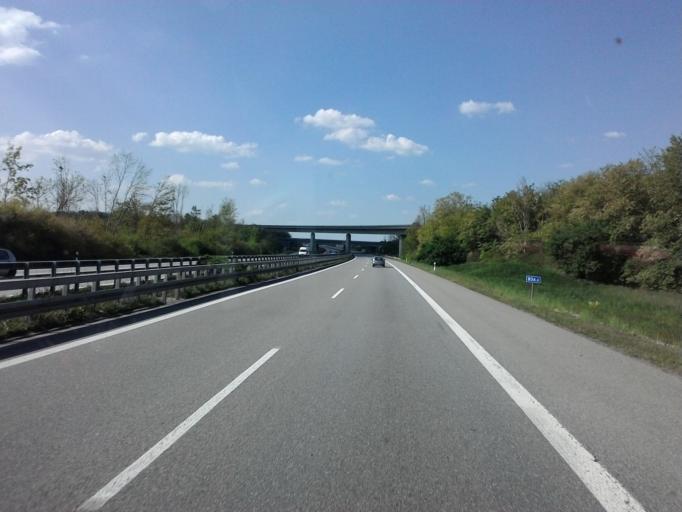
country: DE
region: Bavaria
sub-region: Swabia
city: Nersingen
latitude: 48.4613
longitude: 10.1169
